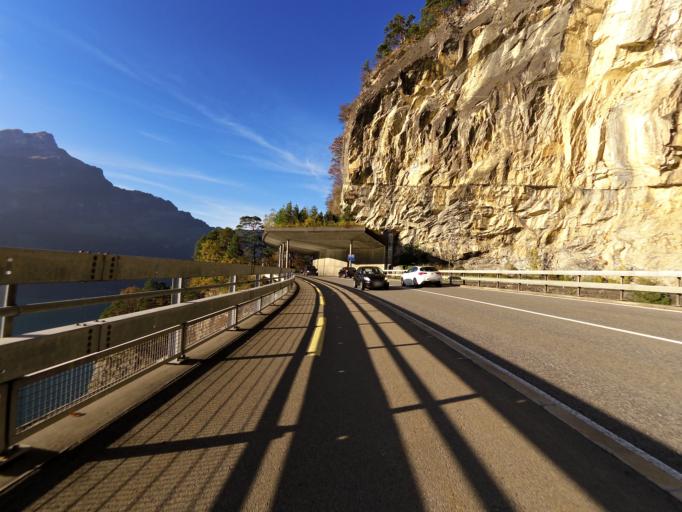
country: CH
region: Uri
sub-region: Uri
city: Flueelen
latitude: 46.9276
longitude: 8.6129
